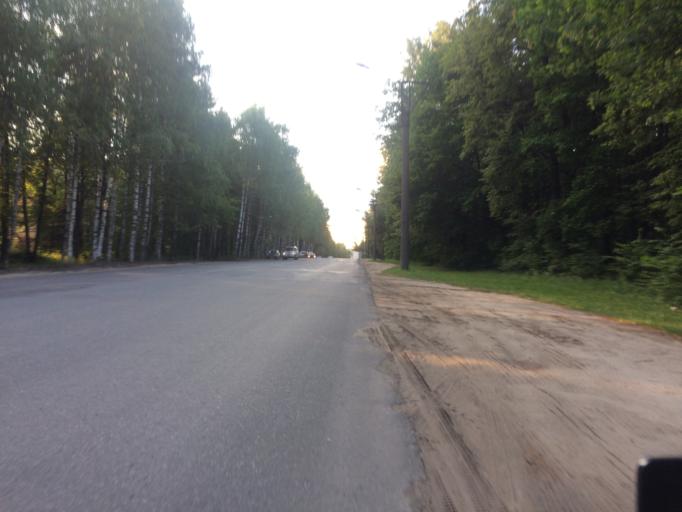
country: RU
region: Mariy-El
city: Yoshkar-Ola
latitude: 56.6235
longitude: 47.9545
